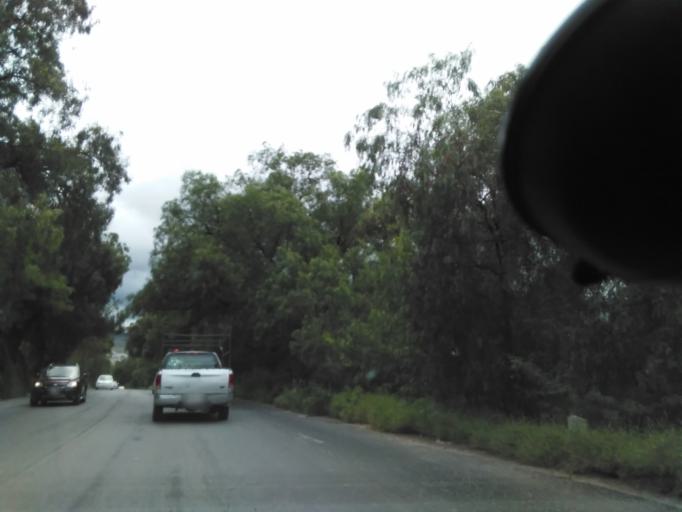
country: MX
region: Hidalgo
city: San Marcos
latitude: 20.0563
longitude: -99.3307
